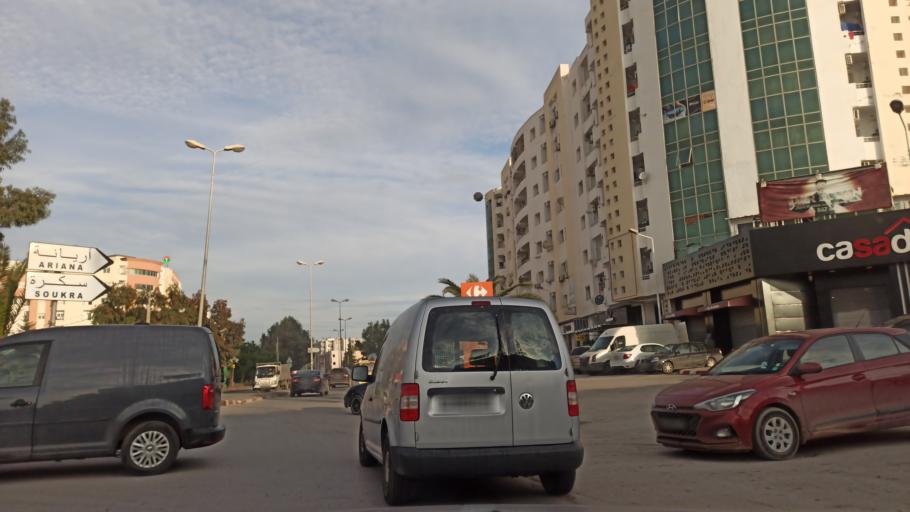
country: TN
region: Ariana
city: Ariana
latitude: 36.8586
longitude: 10.2562
